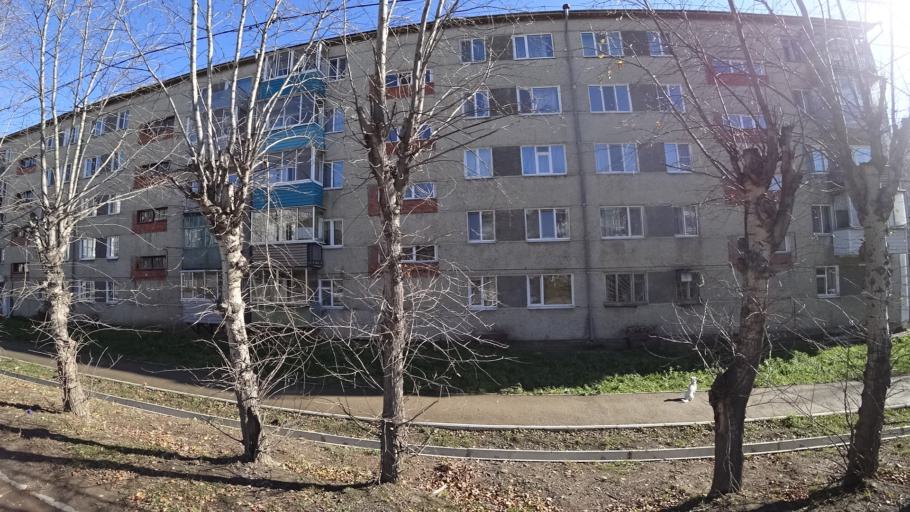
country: RU
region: Khabarovsk Krai
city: Amursk
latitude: 50.2170
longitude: 136.8932
